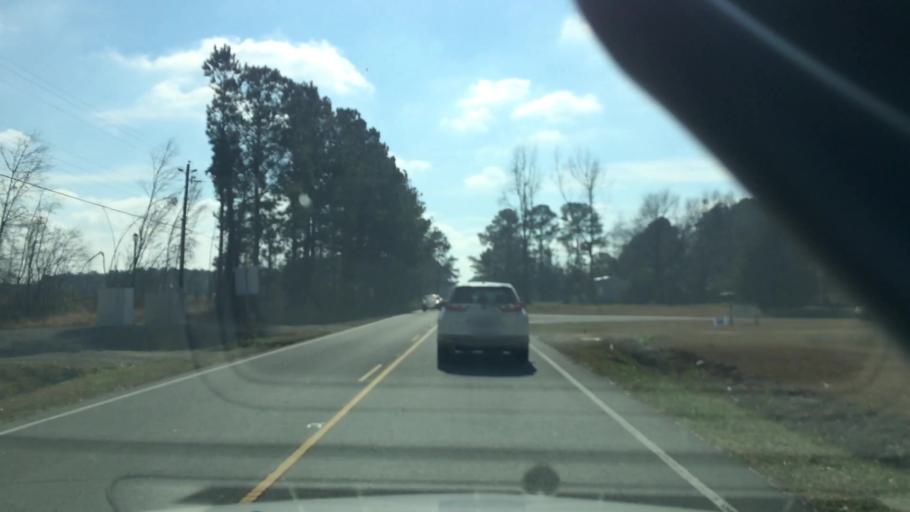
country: US
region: North Carolina
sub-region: Duplin County
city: Beulaville
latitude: 34.8759
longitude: -77.7905
